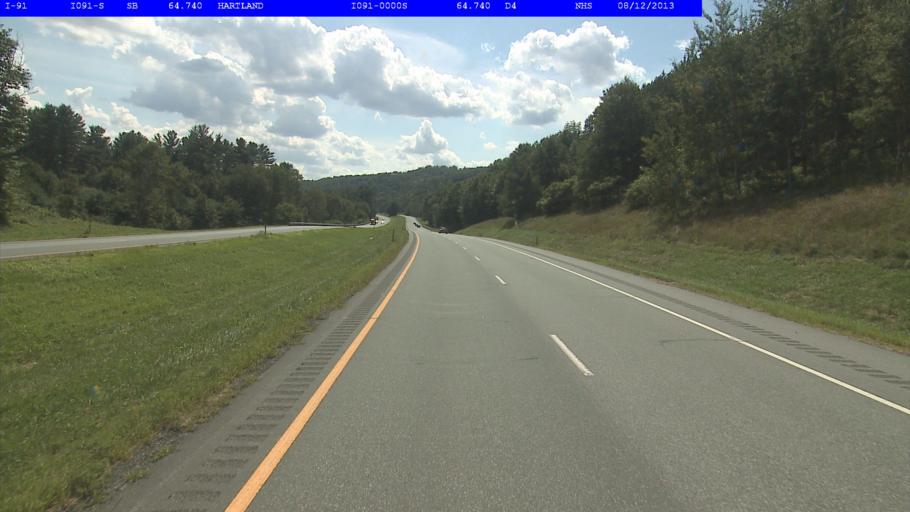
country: US
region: Vermont
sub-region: Windsor County
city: White River Junction
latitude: 43.5840
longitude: -72.3777
